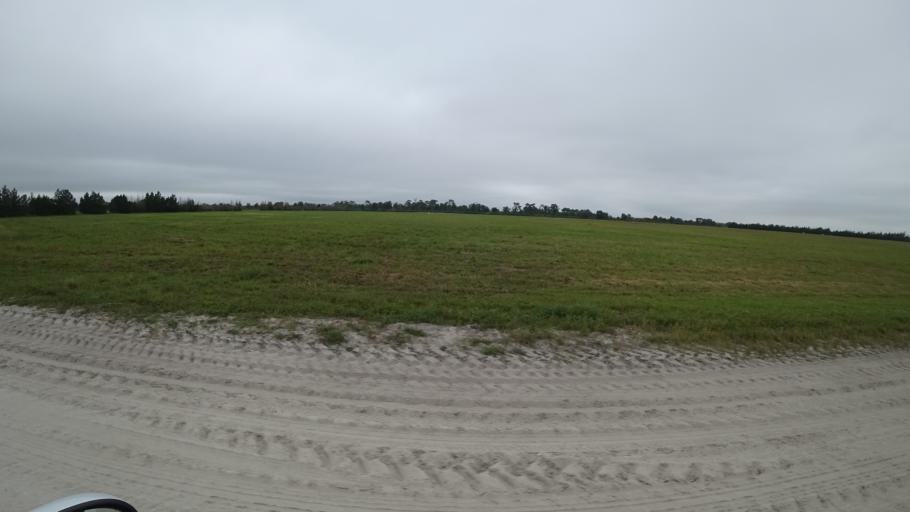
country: US
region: Florida
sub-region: Sarasota County
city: Warm Mineral Springs
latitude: 27.2998
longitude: -82.1310
